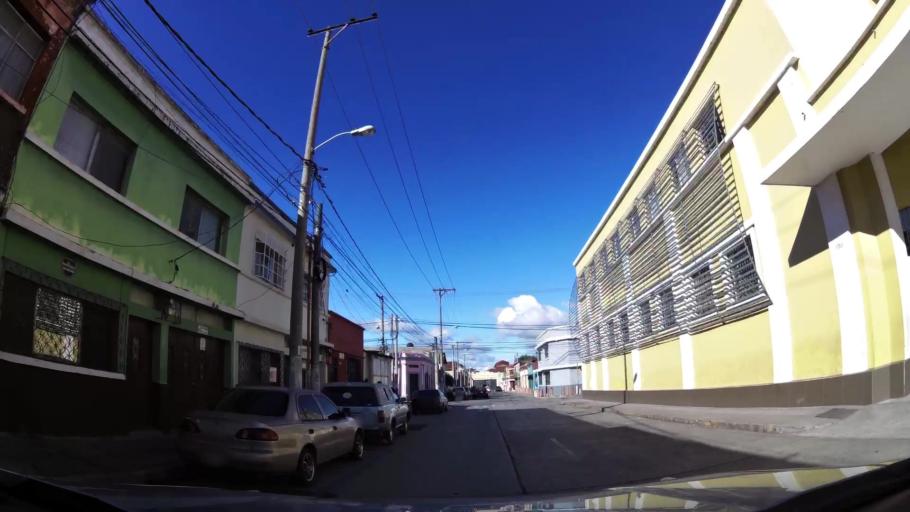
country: GT
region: Guatemala
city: Guatemala City
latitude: 14.6345
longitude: -90.5066
